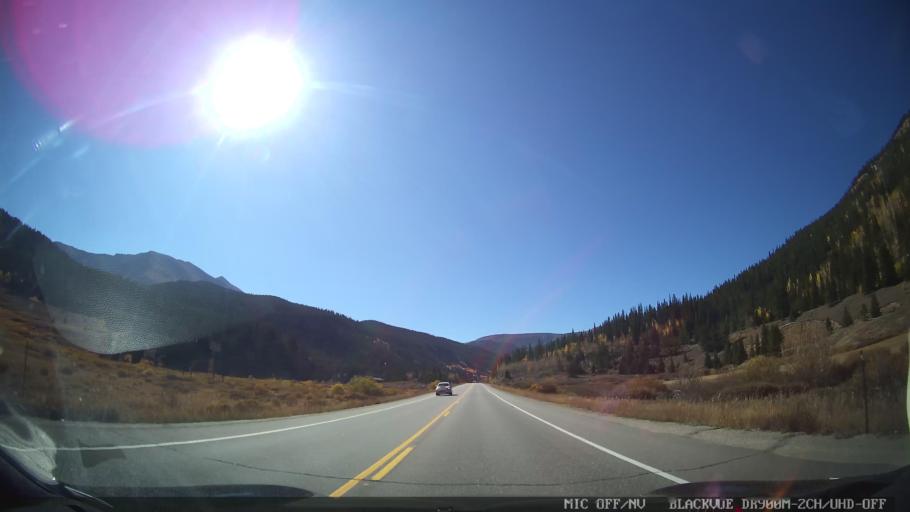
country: US
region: Colorado
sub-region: Lake County
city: Leadville
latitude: 39.3339
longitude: -106.2196
